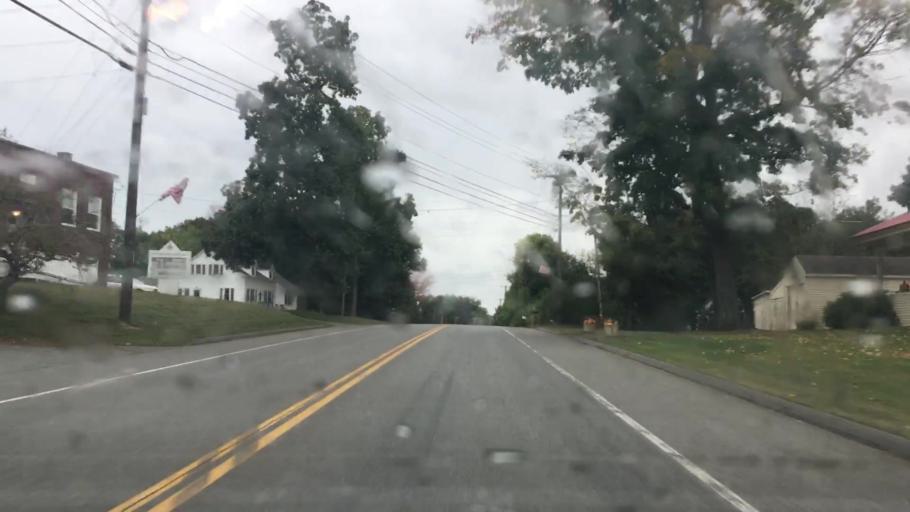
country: US
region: Maine
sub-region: Penobscot County
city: Orrington
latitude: 44.7279
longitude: -68.8273
